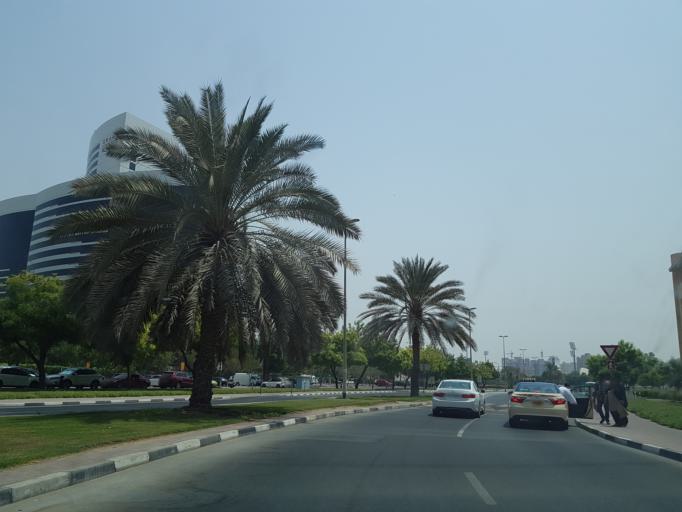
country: AE
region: Ash Shariqah
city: Sharjah
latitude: 25.2302
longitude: 55.3256
